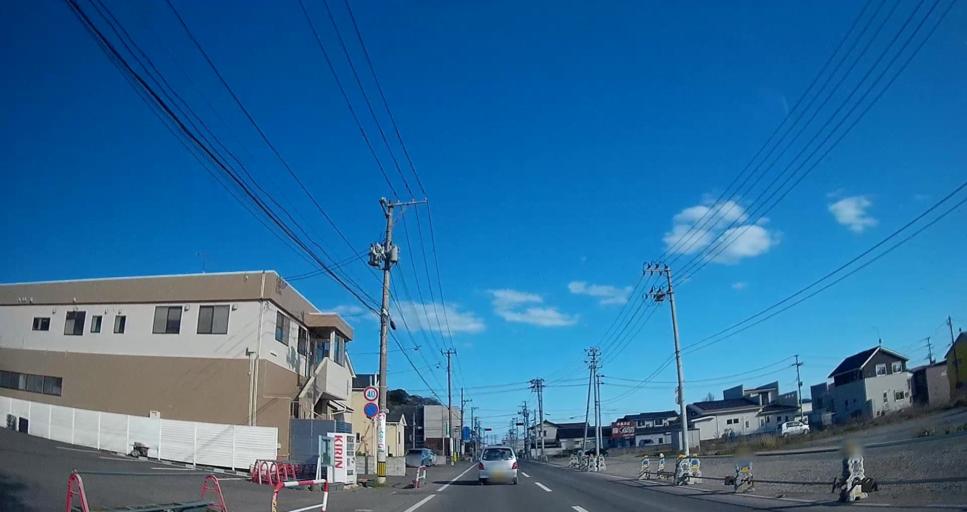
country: JP
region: Miyagi
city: Ishinomaki
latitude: 38.4234
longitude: 141.3193
